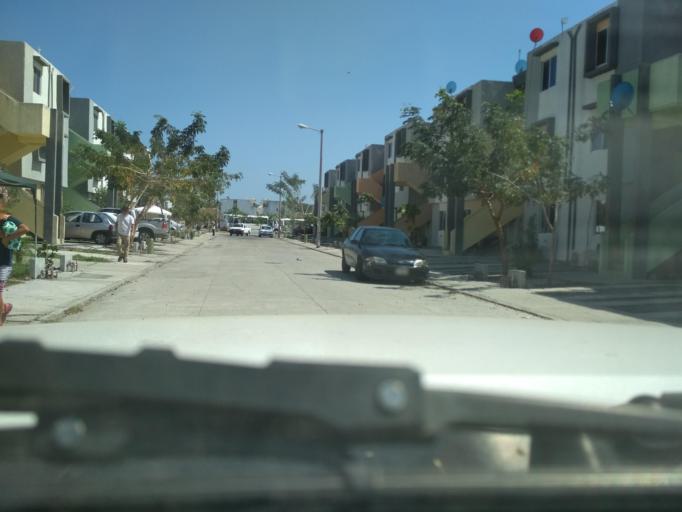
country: MX
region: Veracruz
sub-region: Medellin
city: Fraccionamiento Arboledas San Ramon
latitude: 19.0900
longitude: -96.1660
